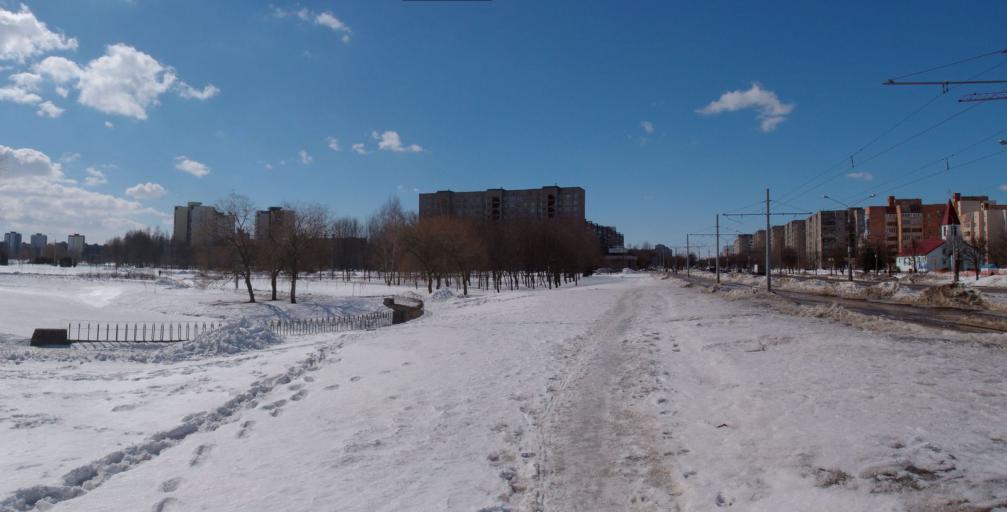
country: BY
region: Minsk
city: Minsk
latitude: 53.8666
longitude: 27.6186
